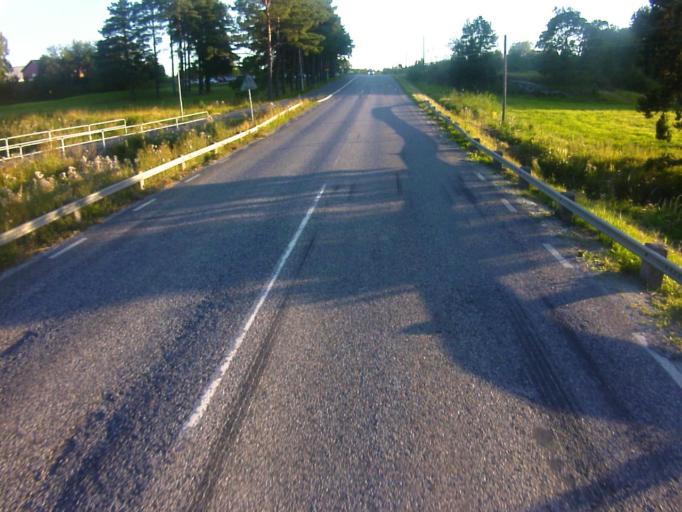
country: SE
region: Soedermanland
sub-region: Eskilstuna Kommun
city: Torshalla
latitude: 59.4140
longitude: 16.4424
